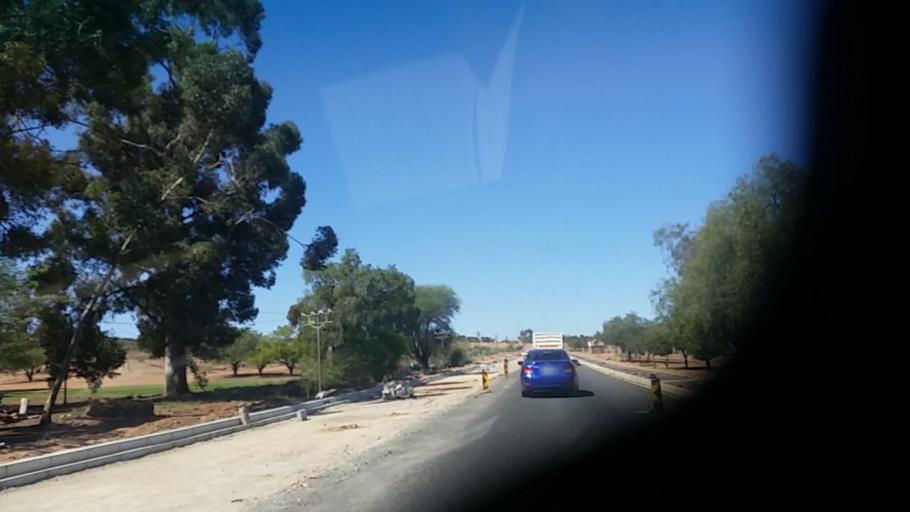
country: ZA
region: Western Cape
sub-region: Eden District Municipality
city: Oudtshoorn
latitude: -33.5941
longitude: 22.2233
